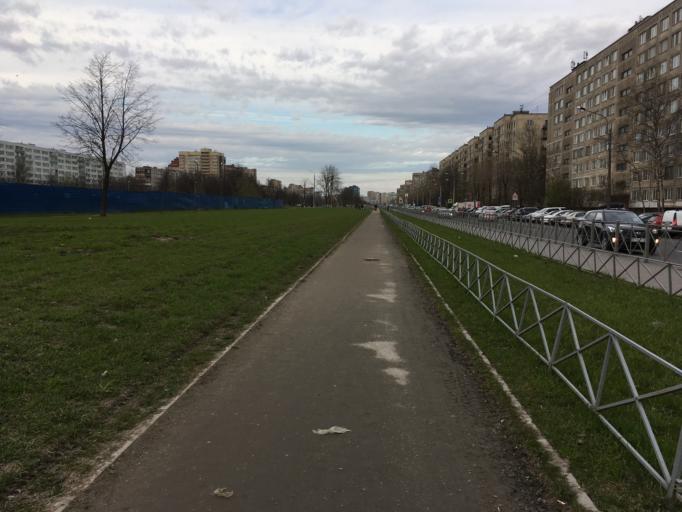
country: RU
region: St.-Petersburg
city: Obukhovo
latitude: 59.8948
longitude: 30.4651
